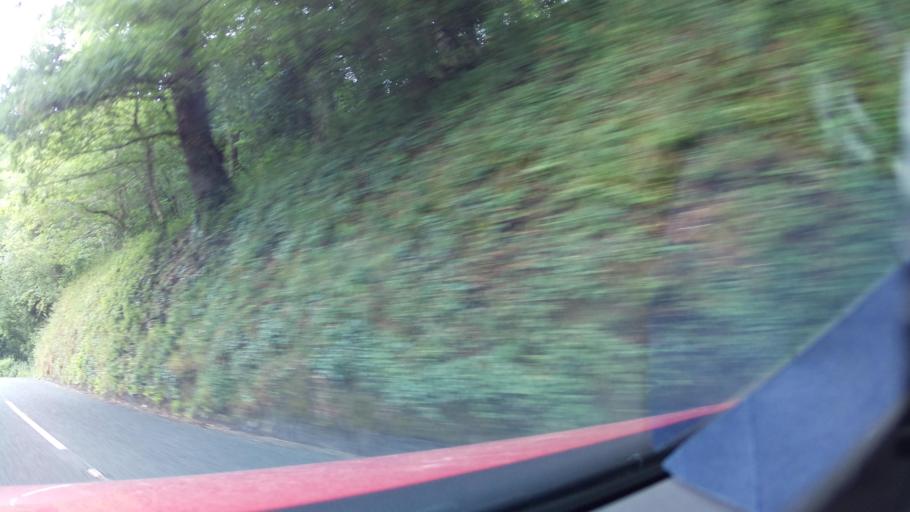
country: GB
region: England
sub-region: Devon
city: Crediton
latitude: 50.6875
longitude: -3.6508
